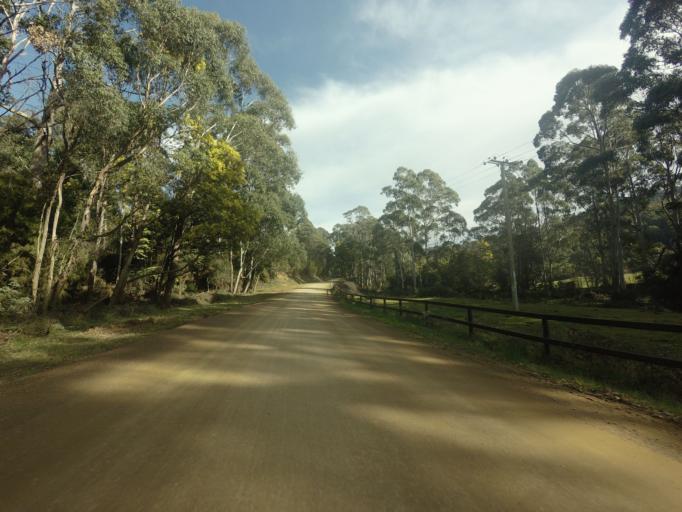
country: AU
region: Tasmania
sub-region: Huon Valley
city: Huonville
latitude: -43.0734
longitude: 147.0801
